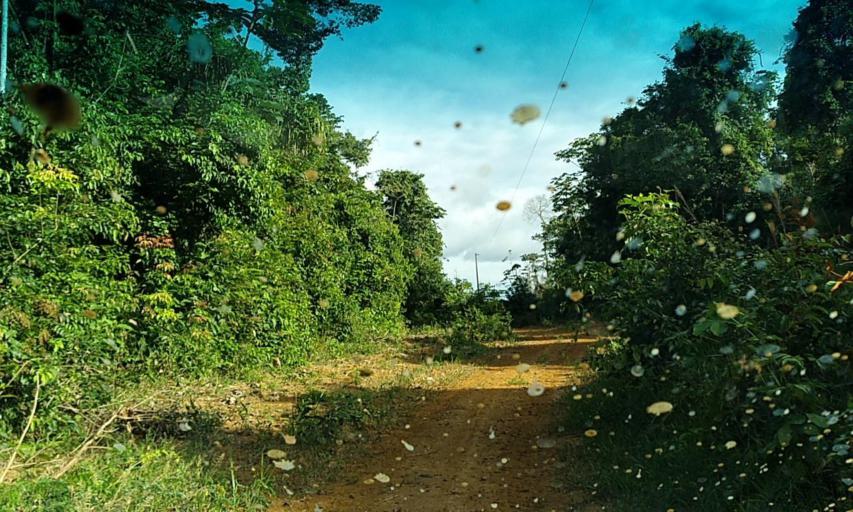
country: BR
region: Para
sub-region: Senador Jose Porfirio
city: Senador Jose Porfirio
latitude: -2.9949
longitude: -51.7432
